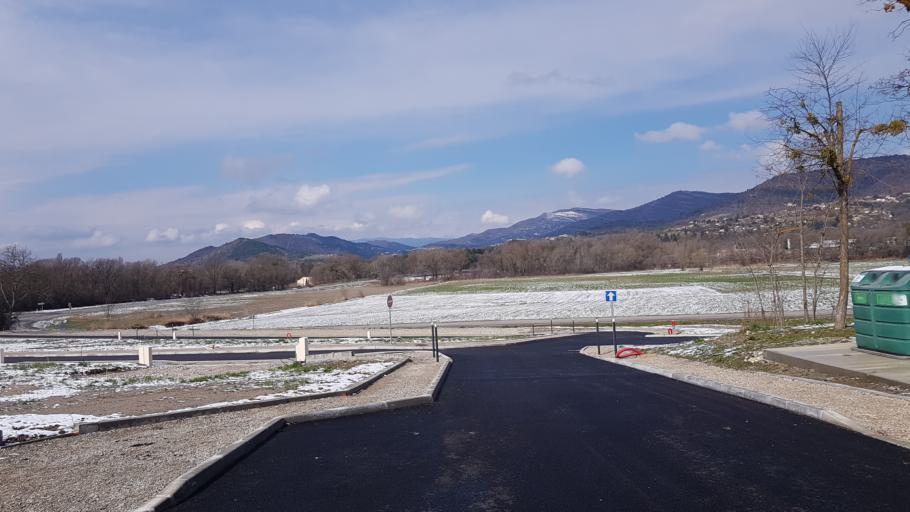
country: FR
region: Provence-Alpes-Cote d'Azur
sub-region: Departement des Alpes-de-Haute-Provence
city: Mallemoisson
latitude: 44.0379
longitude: 6.1492
